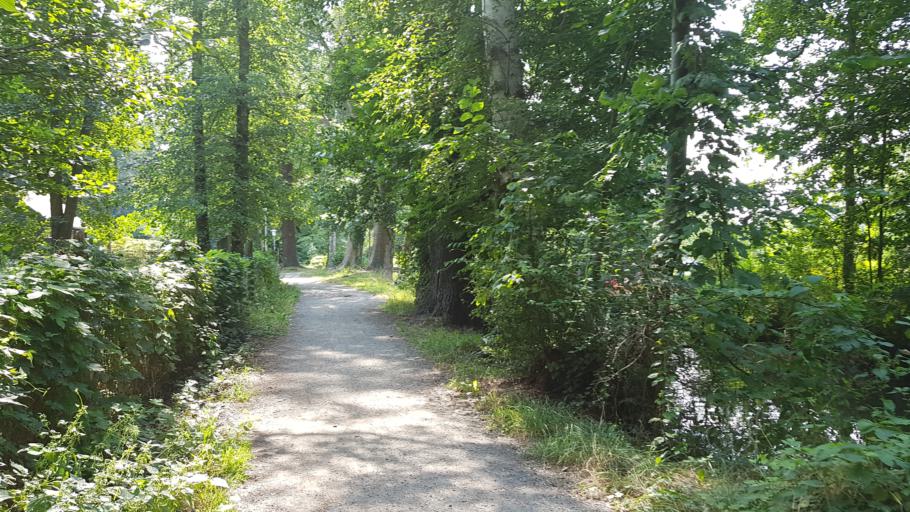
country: DE
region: Brandenburg
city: Lubbenau
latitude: 51.8716
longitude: 13.9717
